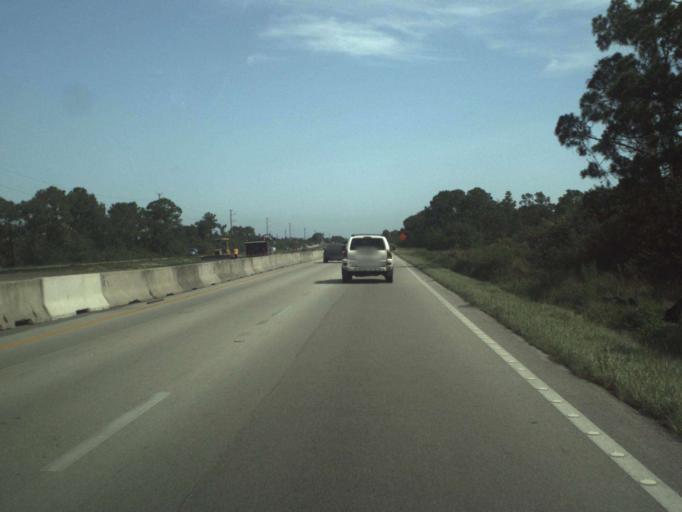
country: US
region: Florida
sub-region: Indian River County
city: West Vero Corridor
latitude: 27.6769
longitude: -80.5324
